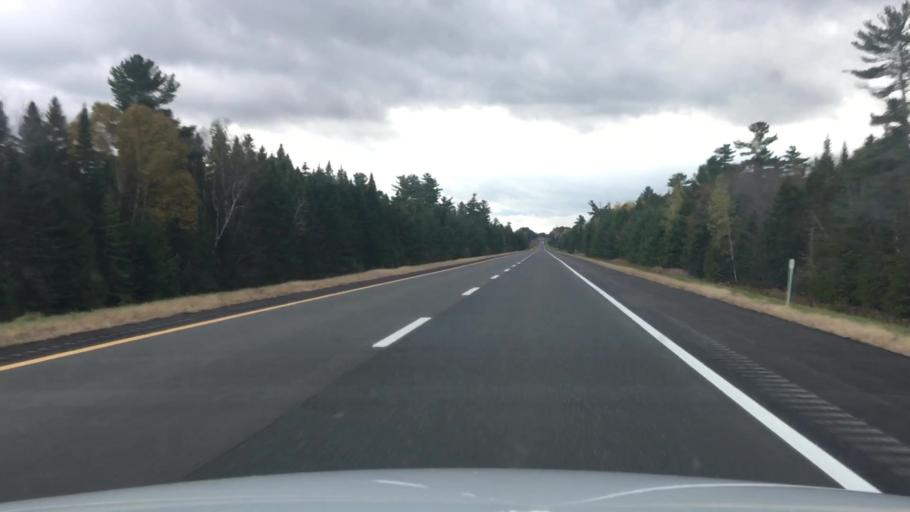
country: US
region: Maine
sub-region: Penobscot County
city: Patten
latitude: 46.0747
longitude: -68.2200
